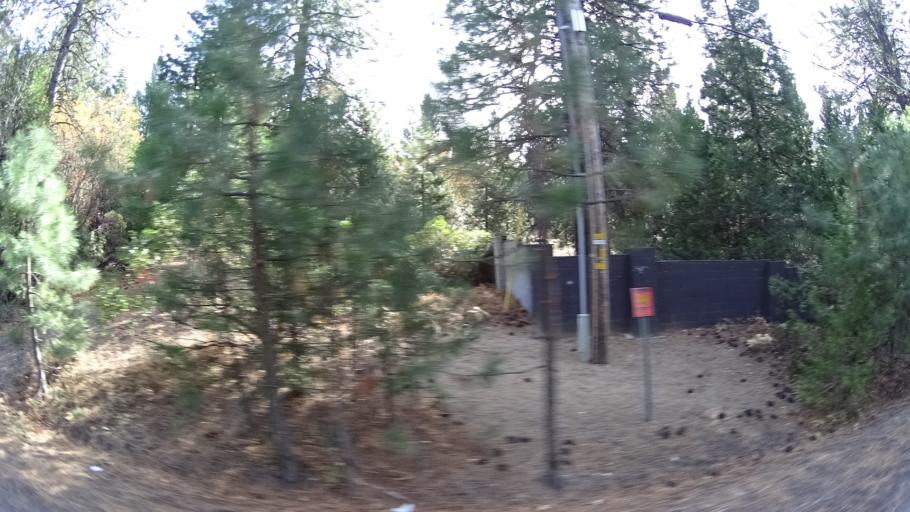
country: US
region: California
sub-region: Siskiyou County
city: Weed
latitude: 41.3819
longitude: -122.3946
